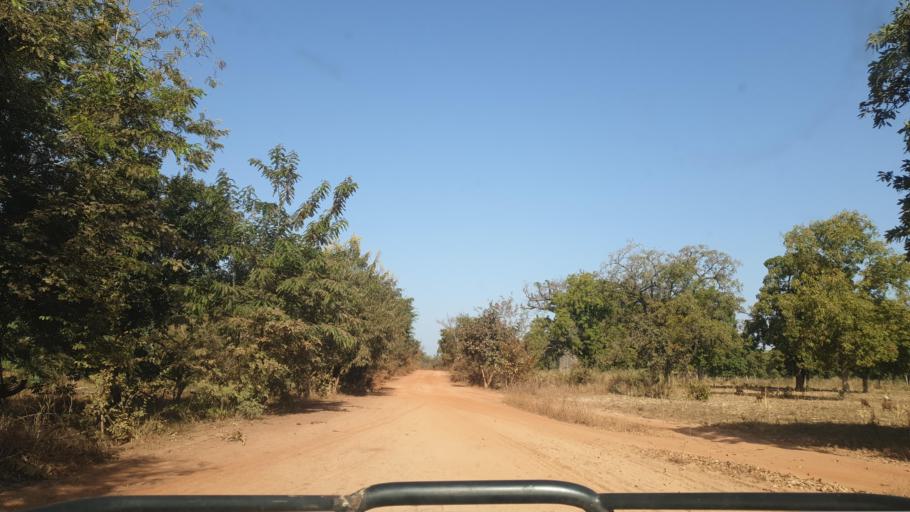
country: ML
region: Sikasso
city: Bougouni
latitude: 11.7741
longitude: -6.9043
